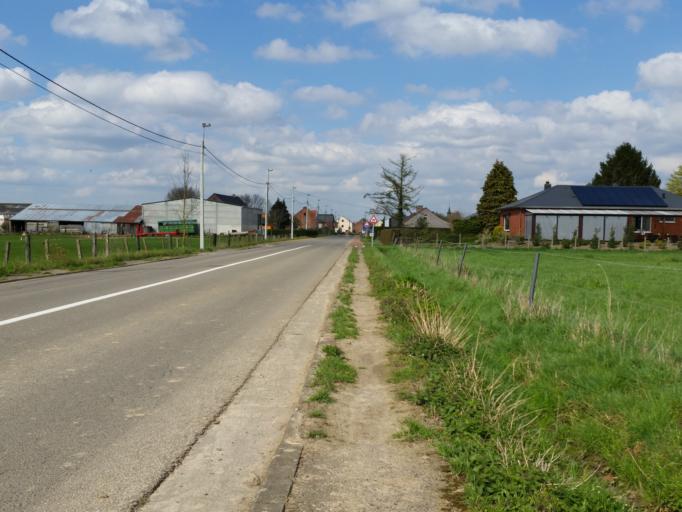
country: BE
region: Flanders
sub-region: Provincie Vlaams-Brabant
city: Haacht
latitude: 50.9310
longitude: 4.6163
